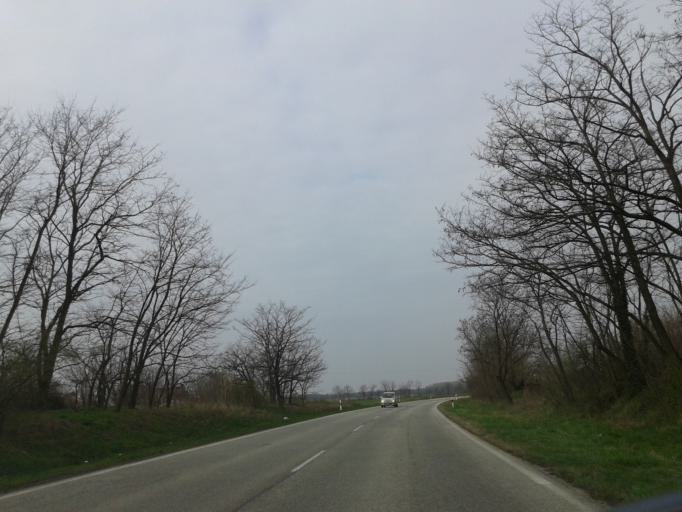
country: HU
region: Komarom-Esztergom
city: Acs
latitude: 47.7261
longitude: 17.9985
